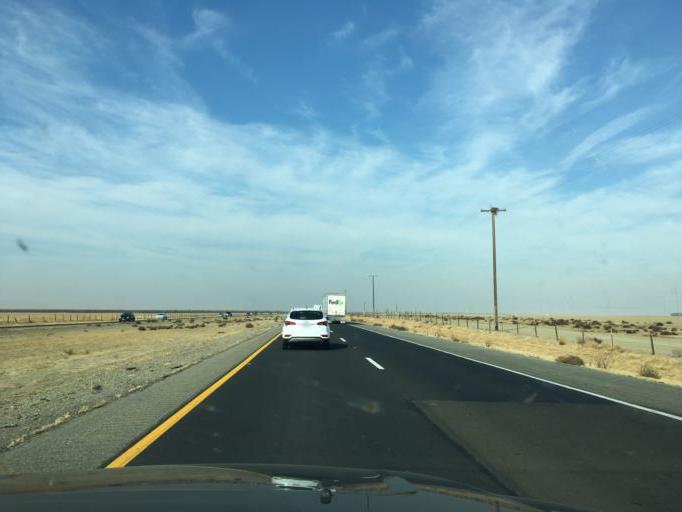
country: US
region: California
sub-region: Kings County
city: Kettleman City
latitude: 35.8916
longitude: -119.8680
